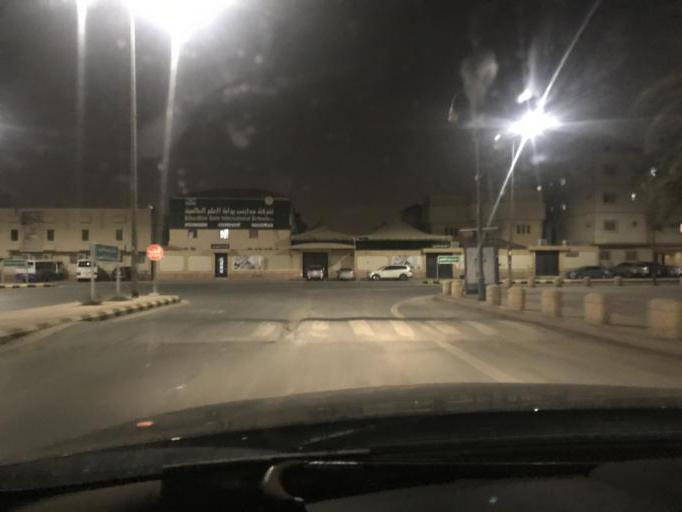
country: SA
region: Ar Riyad
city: Riyadh
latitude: 24.7314
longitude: 46.7773
